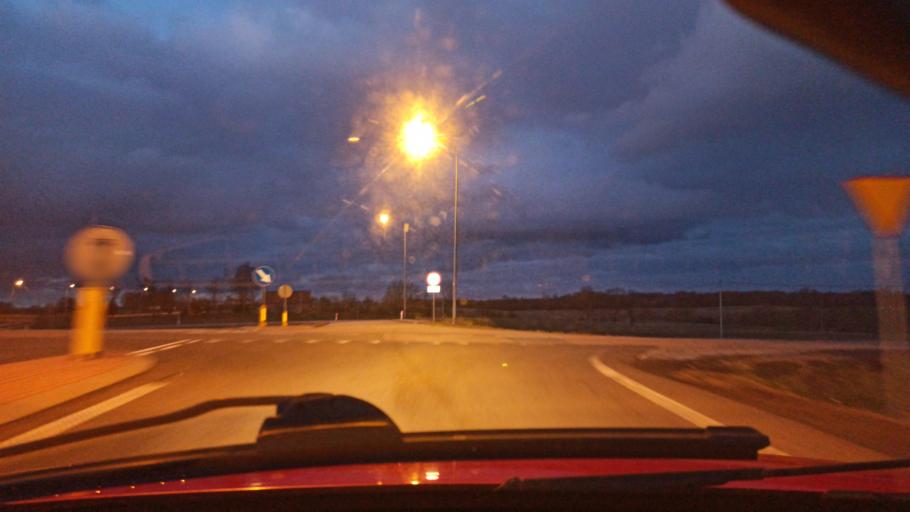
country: PL
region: Warmian-Masurian Voivodeship
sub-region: Powiat elblaski
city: Gronowo Gorne
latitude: 54.1684
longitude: 19.5310
